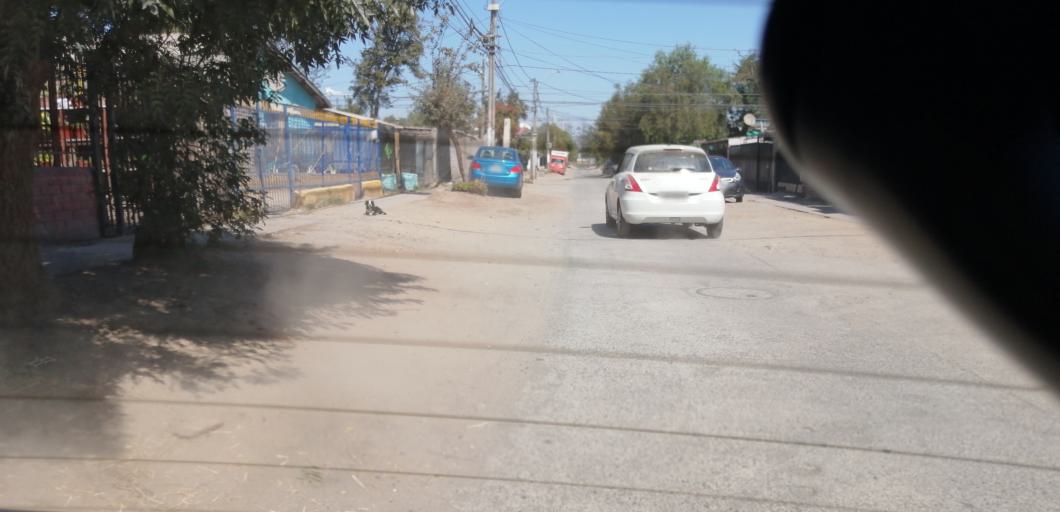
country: CL
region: Santiago Metropolitan
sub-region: Provincia de Santiago
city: Lo Prado
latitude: -33.4482
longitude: -70.7489
